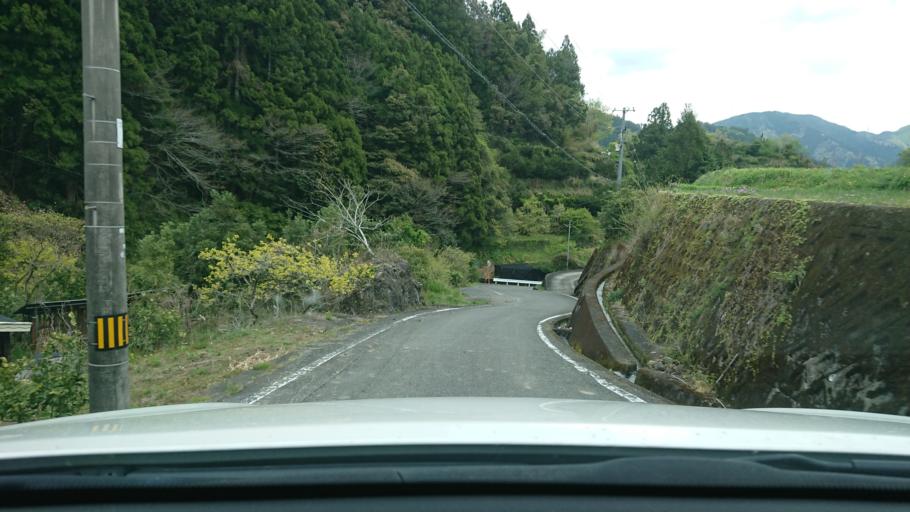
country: JP
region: Tokushima
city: Kamojimacho-jogejima
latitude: 33.8876
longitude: 134.3951
